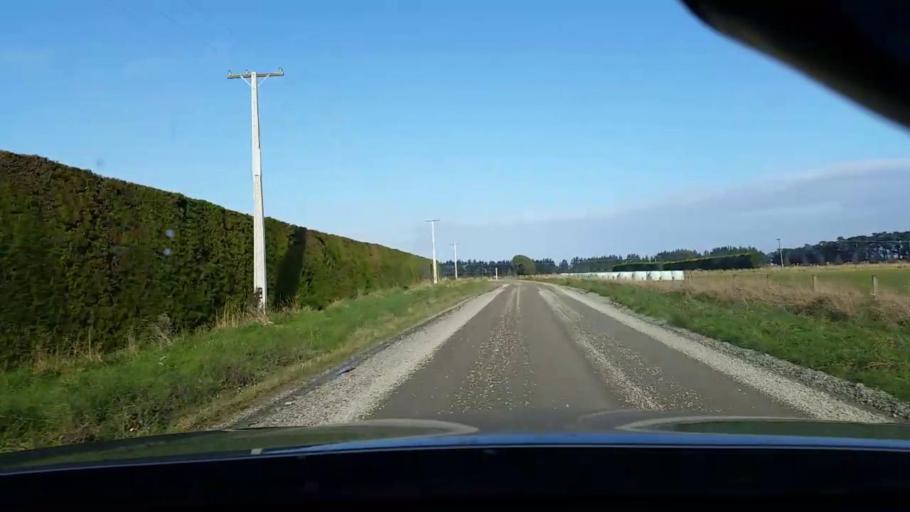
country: NZ
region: Southland
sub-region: Invercargill City
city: Invercargill
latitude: -46.2931
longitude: 168.2947
